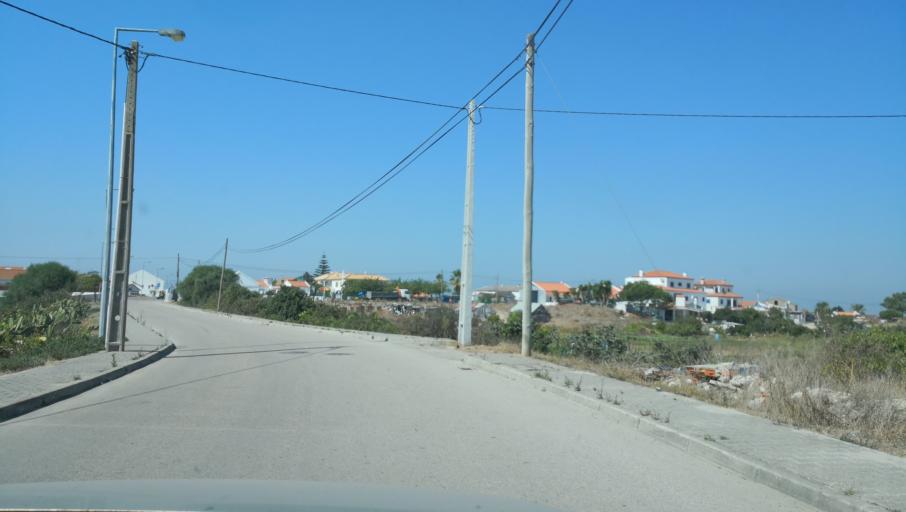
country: PT
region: Setubal
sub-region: Setubal
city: Setubal
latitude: 38.4088
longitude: -8.7487
